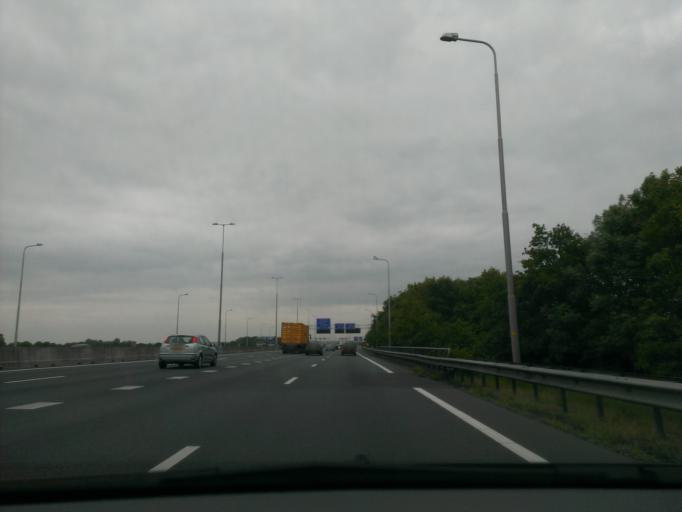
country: NL
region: Gelderland
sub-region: Gemeente Apeldoorn
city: Apeldoorn
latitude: 52.1937
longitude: 6.0366
